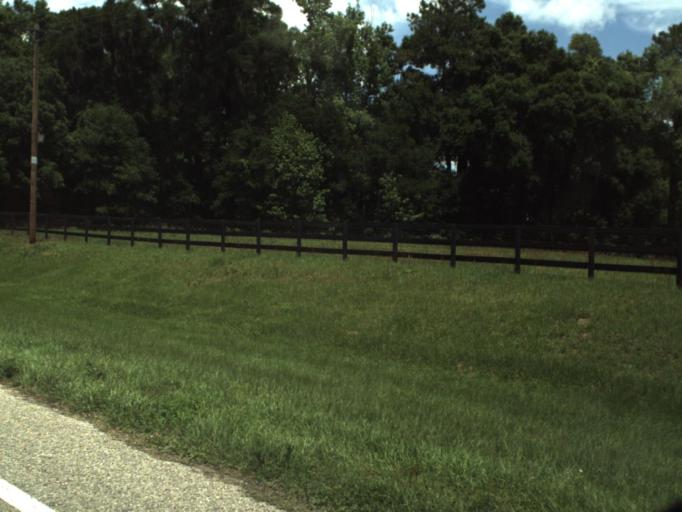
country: US
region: Florida
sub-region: Marion County
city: Citra
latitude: 29.3951
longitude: -82.1960
